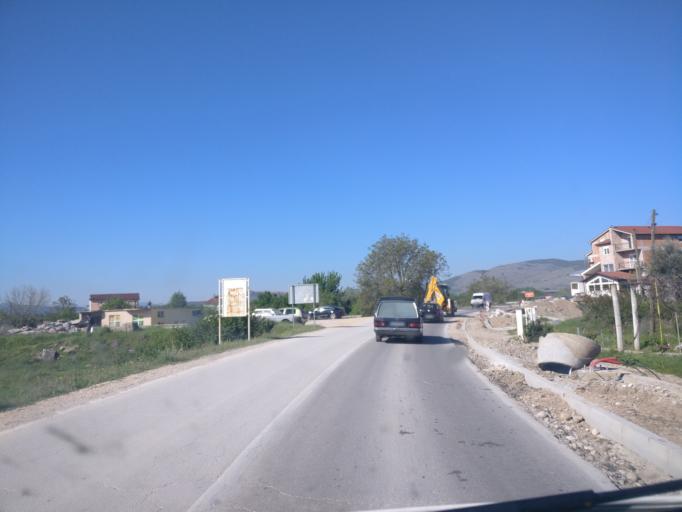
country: BA
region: Federation of Bosnia and Herzegovina
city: Tasovcici
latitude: 43.1083
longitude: 17.7195
